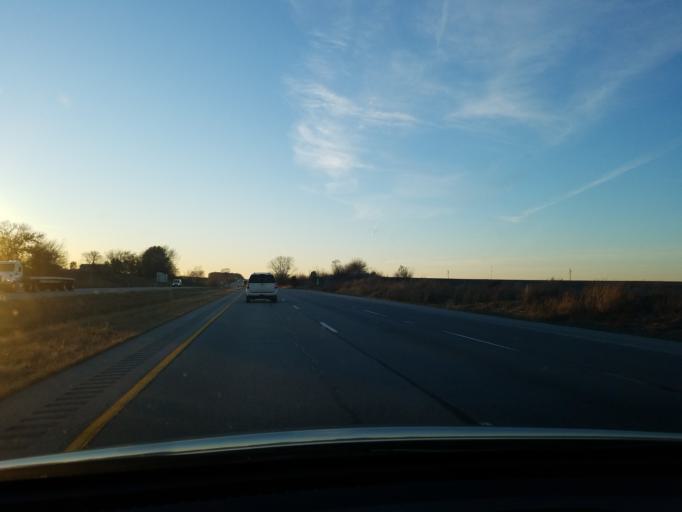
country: US
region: Indiana
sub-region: Posey County
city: Poseyville
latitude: 38.1842
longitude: -87.7862
